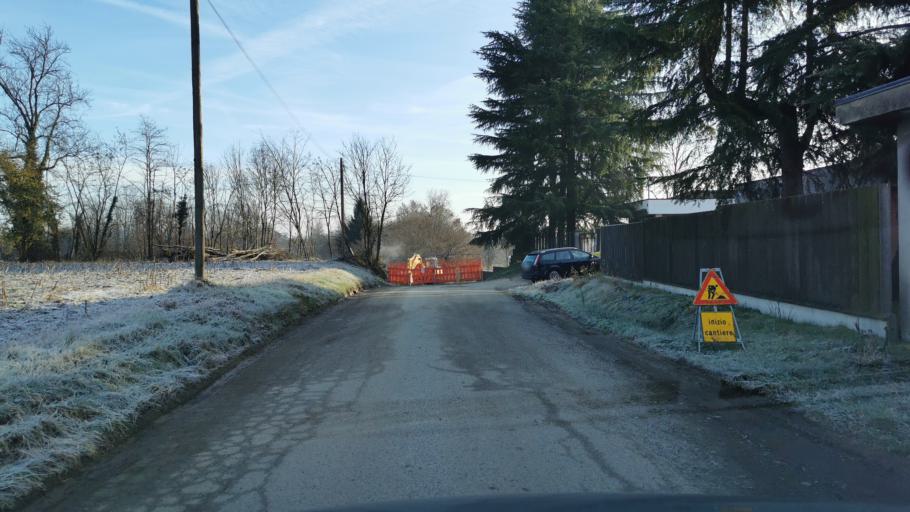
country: IT
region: Piedmont
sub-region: Provincia di Torino
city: Bosconero
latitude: 45.2860
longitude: 7.7632
